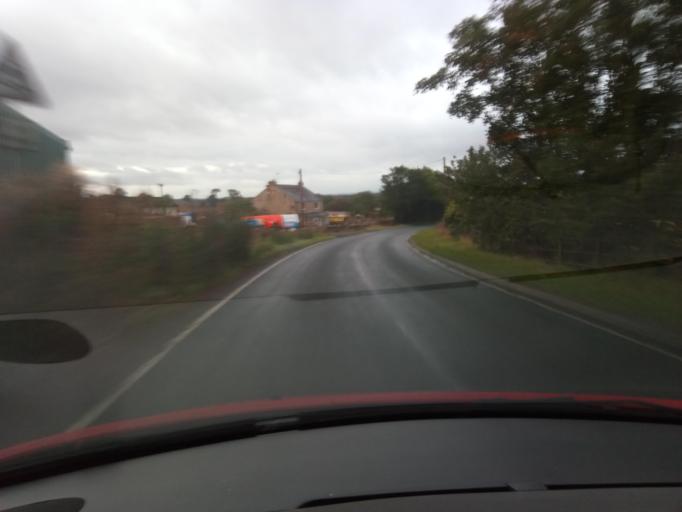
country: GB
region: England
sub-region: Darlington
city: High Coniscliffe
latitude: 54.4752
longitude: -1.6704
